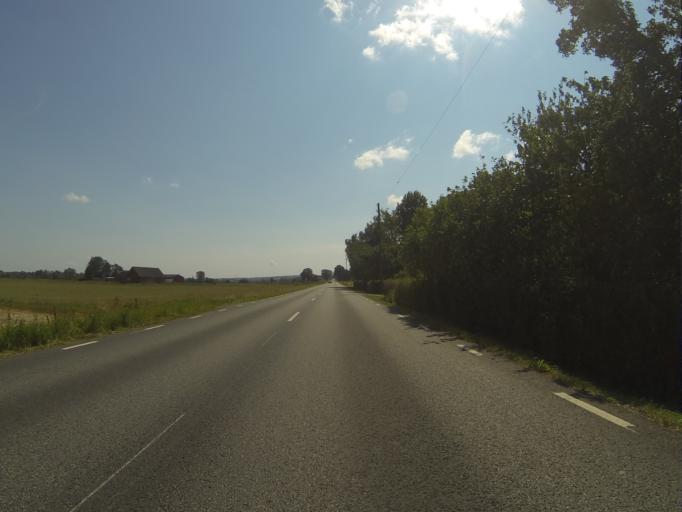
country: SE
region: Skane
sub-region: Eslovs Kommun
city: Eslov
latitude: 55.7490
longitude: 13.3244
